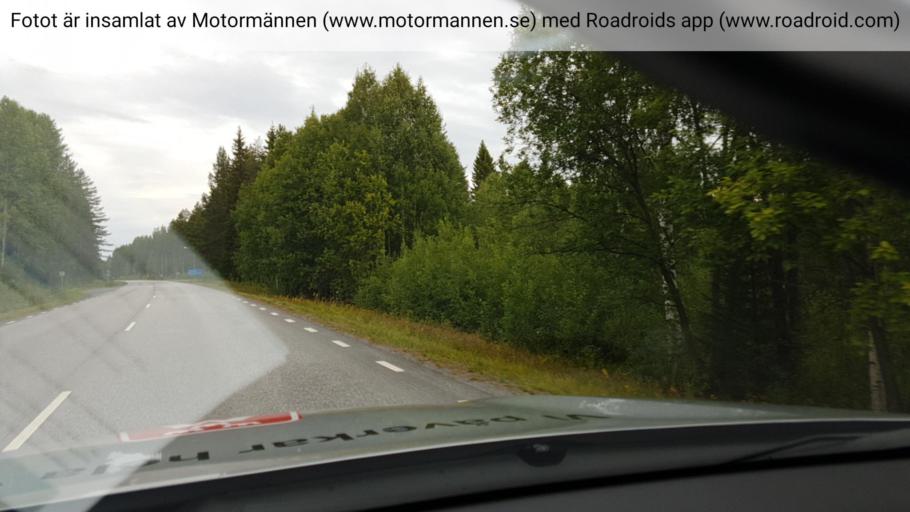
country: SE
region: Norrbotten
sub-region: Bodens Kommun
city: Boden
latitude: 65.8060
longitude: 21.6563
